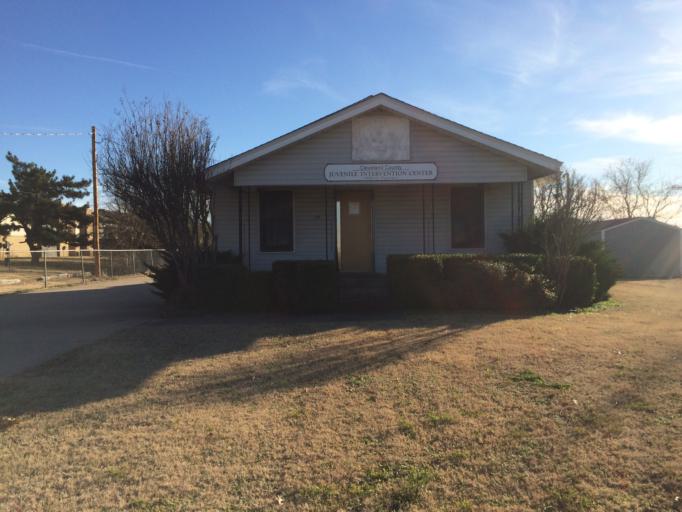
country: US
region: Oklahoma
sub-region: Cleveland County
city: Norman
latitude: 35.2328
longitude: -97.4686
